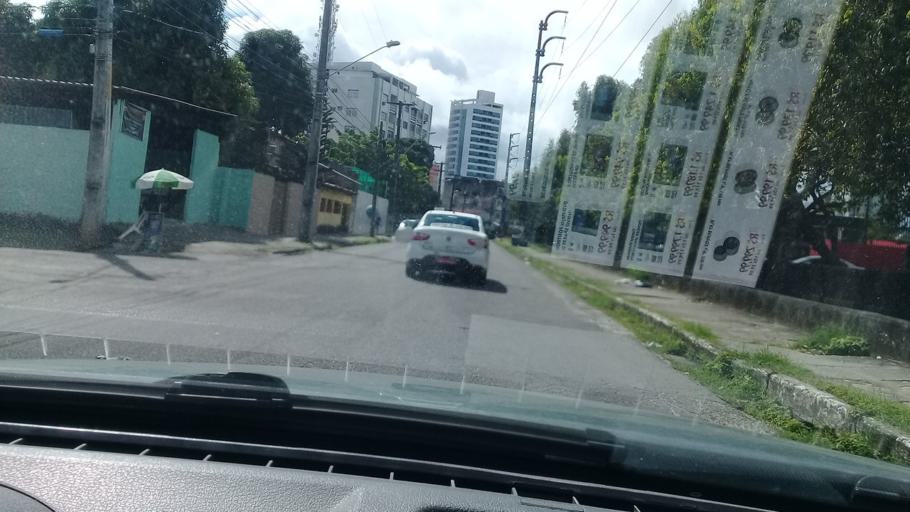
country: BR
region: Pernambuco
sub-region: Recife
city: Recife
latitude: -8.0638
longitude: -34.9047
